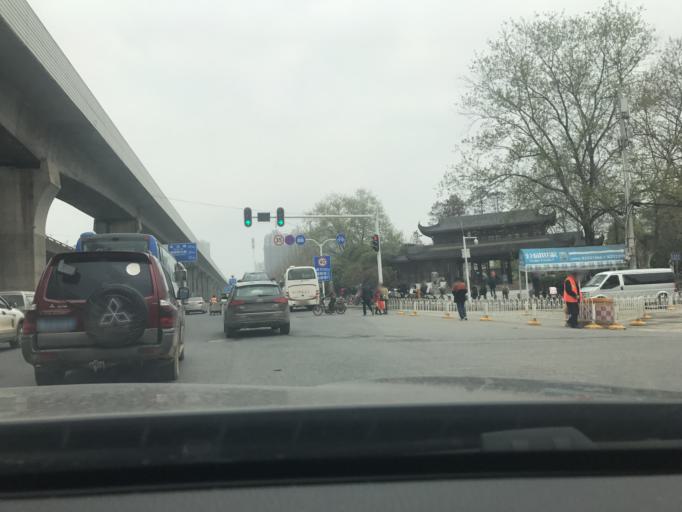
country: CN
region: Hubei
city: Houhu
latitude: 30.6606
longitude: 114.3300
